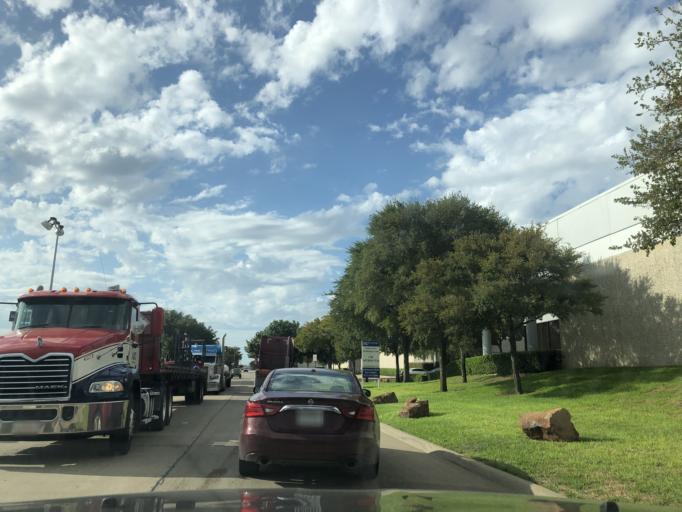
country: US
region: Texas
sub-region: Dallas County
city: Garland
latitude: 32.8841
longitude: -96.6673
